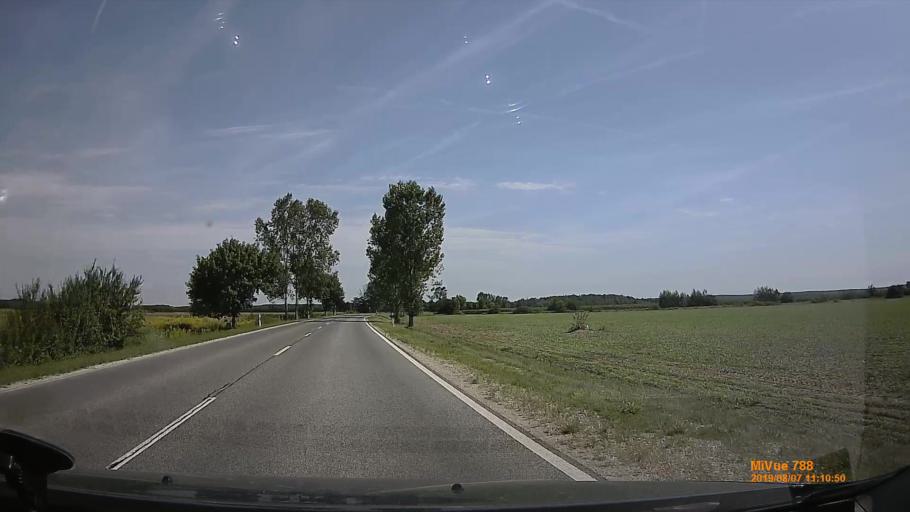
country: HU
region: Zala
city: Lenti
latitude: 46.6711
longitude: 16.5140
